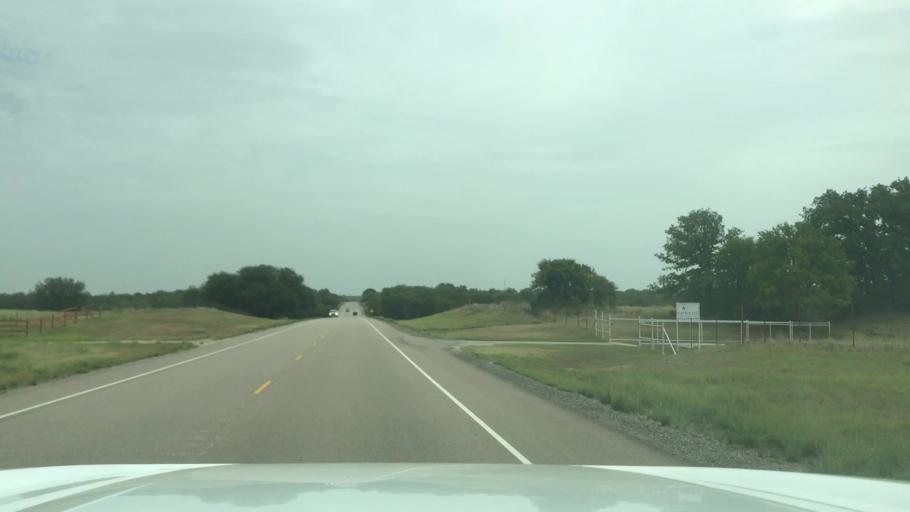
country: US
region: Texas
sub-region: Hamilton County
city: Hico
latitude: 31.9778
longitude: -97.9013
